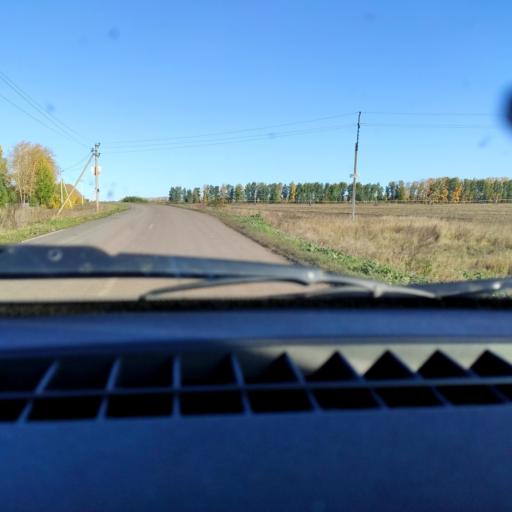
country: RU
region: Bashkortostan
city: Avdon
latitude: 54.5144
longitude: 55.7739
